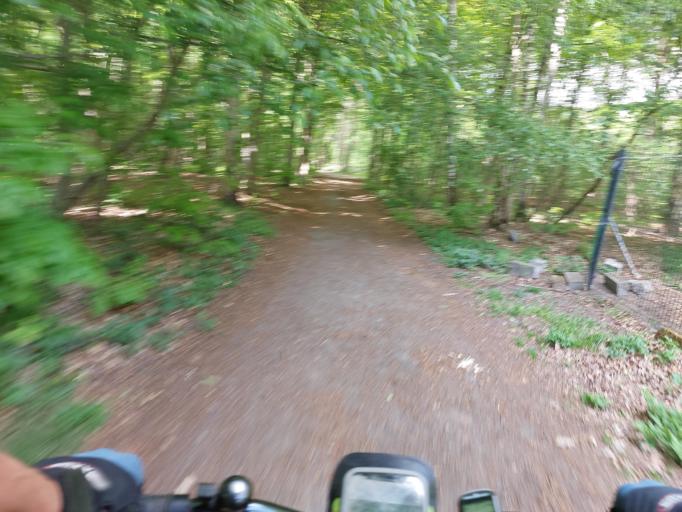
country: BE
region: Wallonia
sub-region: Province du Hainaut
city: Jurbise
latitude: 50.5034
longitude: 3.8785
